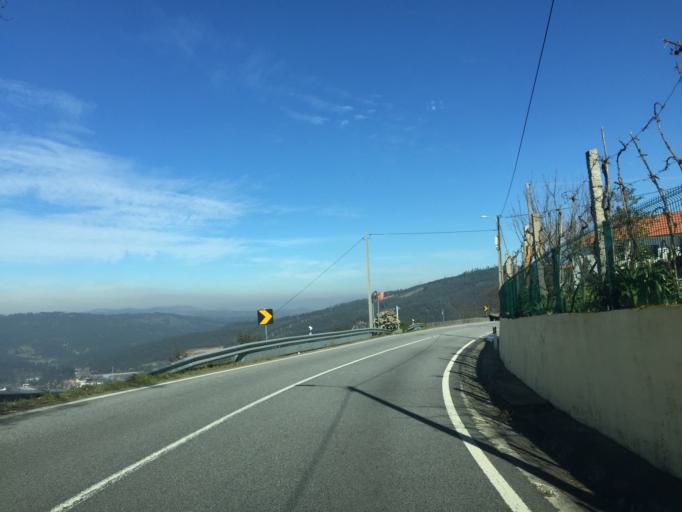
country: PT
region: Aveiro
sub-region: Vale de Cambra
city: Macieira de Cambra
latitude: 40.9066
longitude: -8.3290
